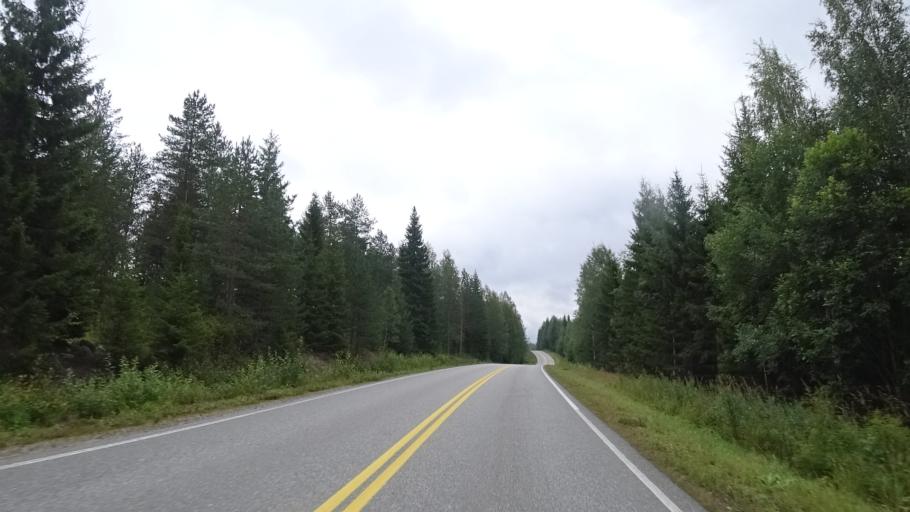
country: FI
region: North Karelia
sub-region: Pielisen Karjala
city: Lieksa
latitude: 63.2817
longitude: 30.5629
